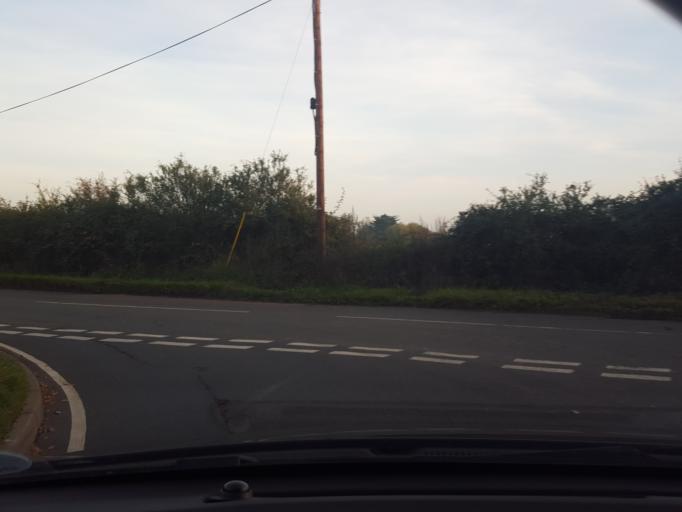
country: GB
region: England
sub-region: Essex
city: Little Clacton
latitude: 51.8265
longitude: 1.1602
